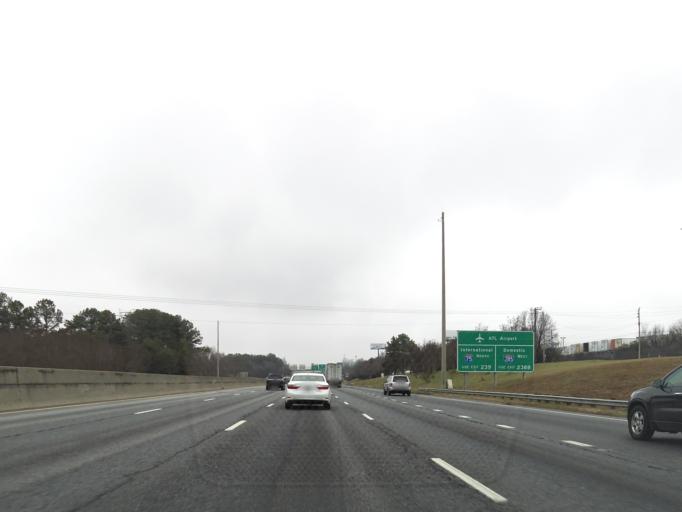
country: US
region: Georgia
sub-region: Clayton County
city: Forest Park
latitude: 33.6249
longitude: -84.4000
